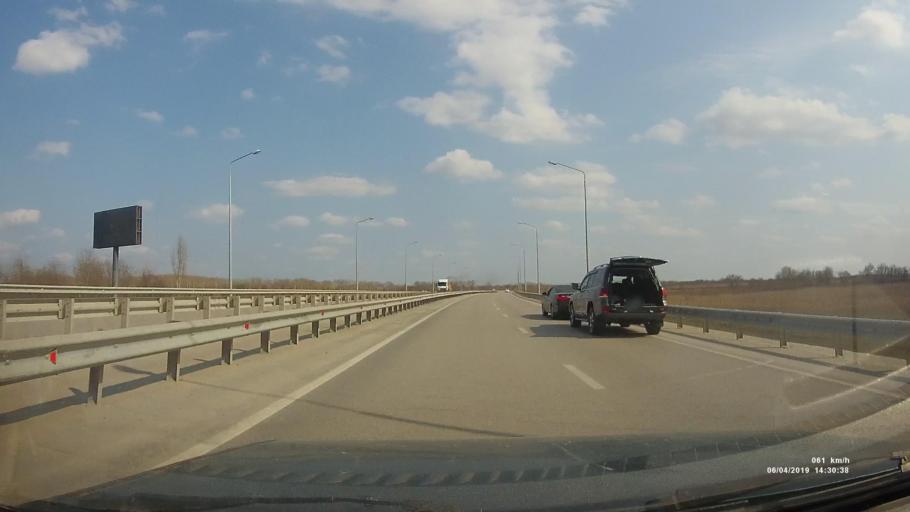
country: RU
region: Rostov
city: Rostov-na-Donu
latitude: 47.2071
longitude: 39.7500
